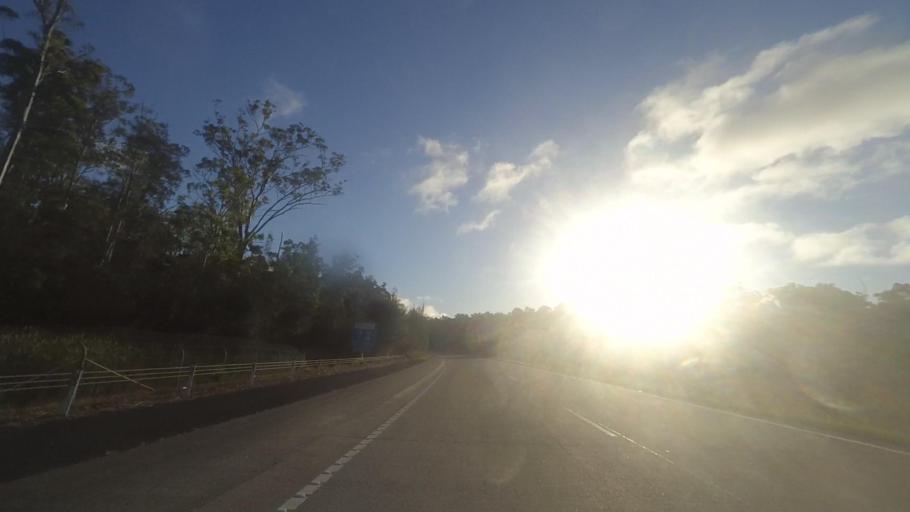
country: AU
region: New South Wales
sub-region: Great Lakes
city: Hawks Nest
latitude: -32.5493
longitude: 152.1536
